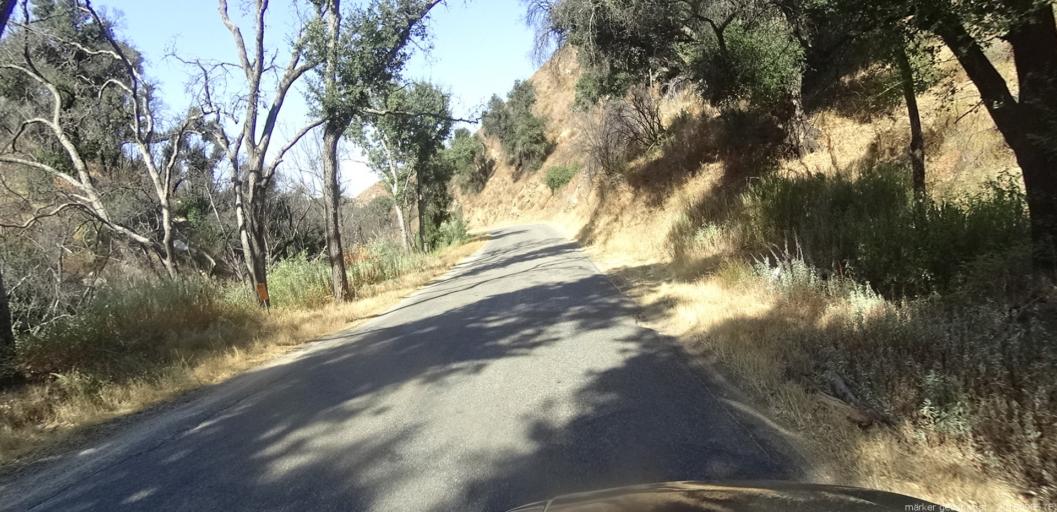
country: US
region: California
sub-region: Monterey County
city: Gonzales
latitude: 36.3925
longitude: -121.5914
